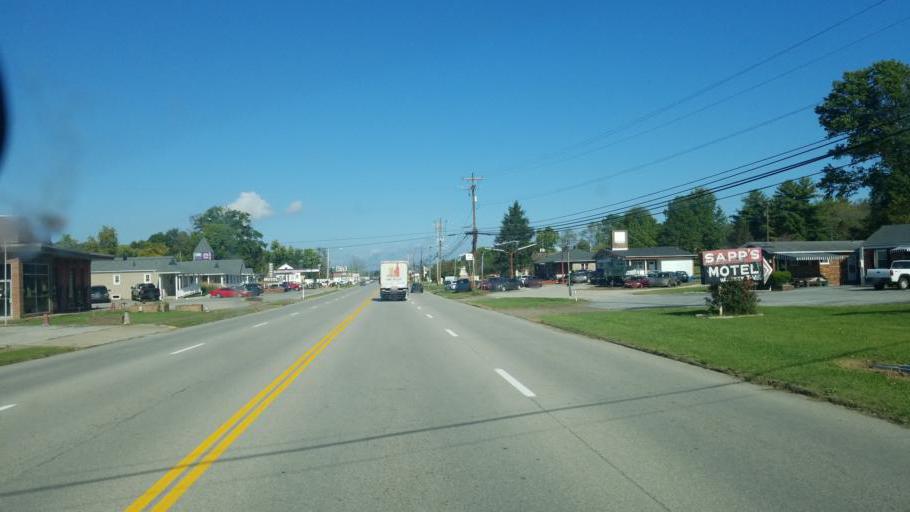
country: US
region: Ohio
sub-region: Brown County
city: Aberdeen
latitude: 38.6578
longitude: -83.7651
